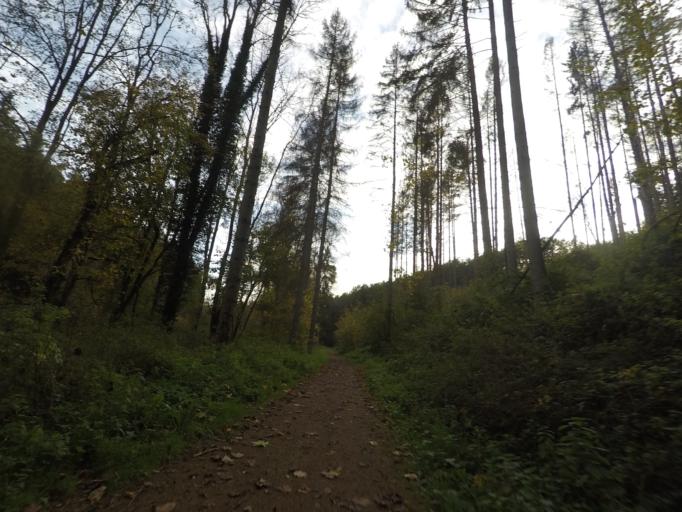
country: LU
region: Luxembourg
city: Itzig
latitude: 49.6001
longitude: 6.1611
